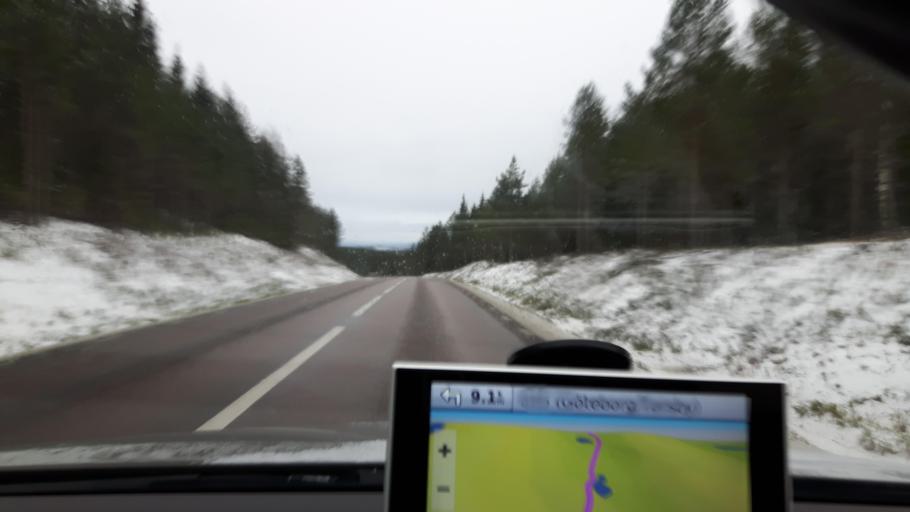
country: SE
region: Vaermland
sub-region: Torsby Kommun
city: Torsby
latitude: 60.3378
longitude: 13.1474
